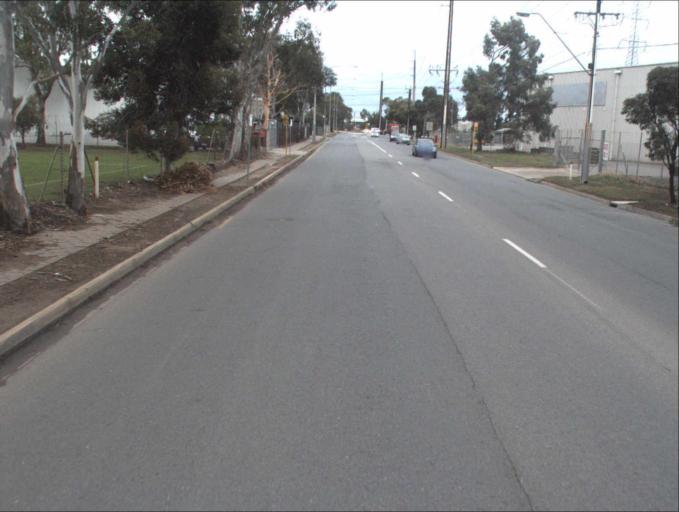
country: AU
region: South Australia
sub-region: Port Adelaide Enfield
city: Enfield
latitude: -34.8392
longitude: 138.5849
